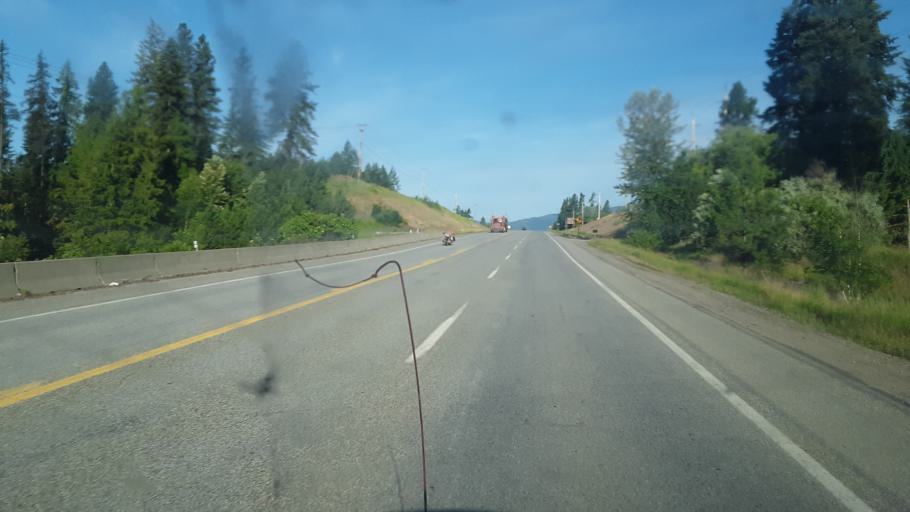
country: US
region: Idaho
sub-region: Boundary County
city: Bonners Ferry
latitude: 48.7317
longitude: -116.2520
